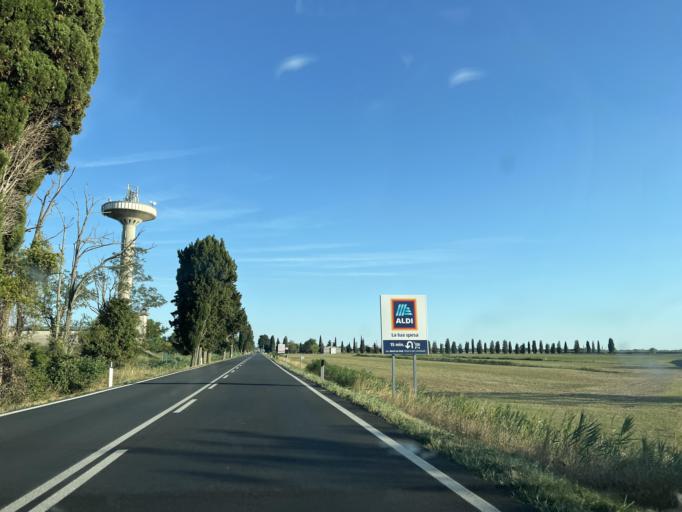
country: IT
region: Friuli Venezia Giulia
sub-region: Provincia di Gorizia
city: Grado
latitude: 45.7208
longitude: 13.4570
